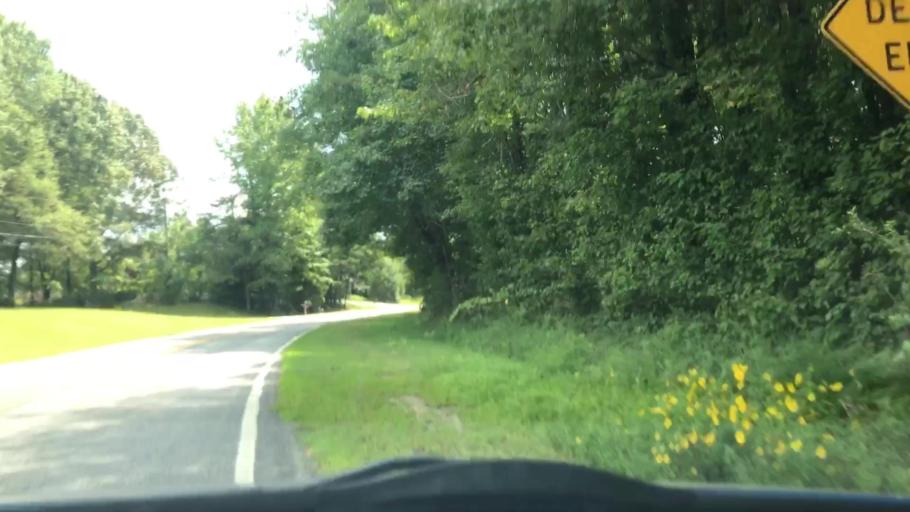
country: US
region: North Carolina
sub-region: Guilford County
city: Pleasant Garden
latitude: 35.9890
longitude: -79.8232
